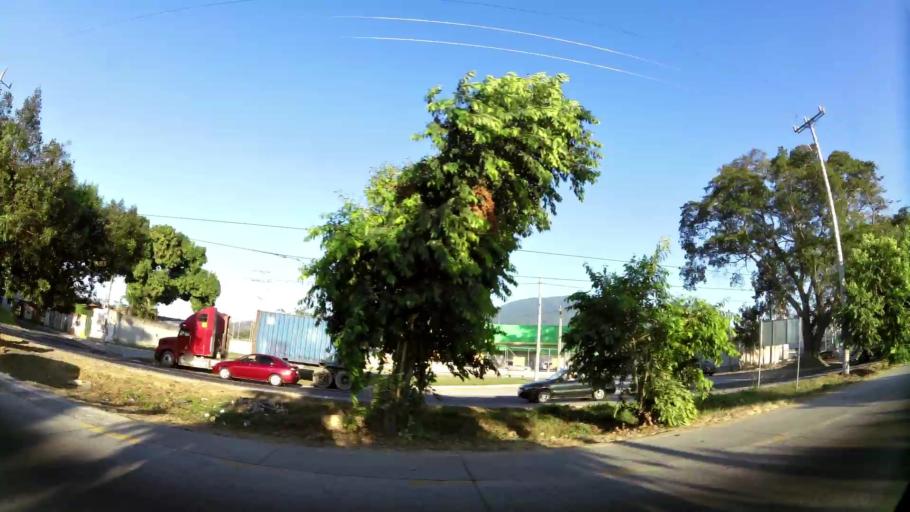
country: SV
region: La Libertad
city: Santa Tecla
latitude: 13.7411
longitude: -89.3626
